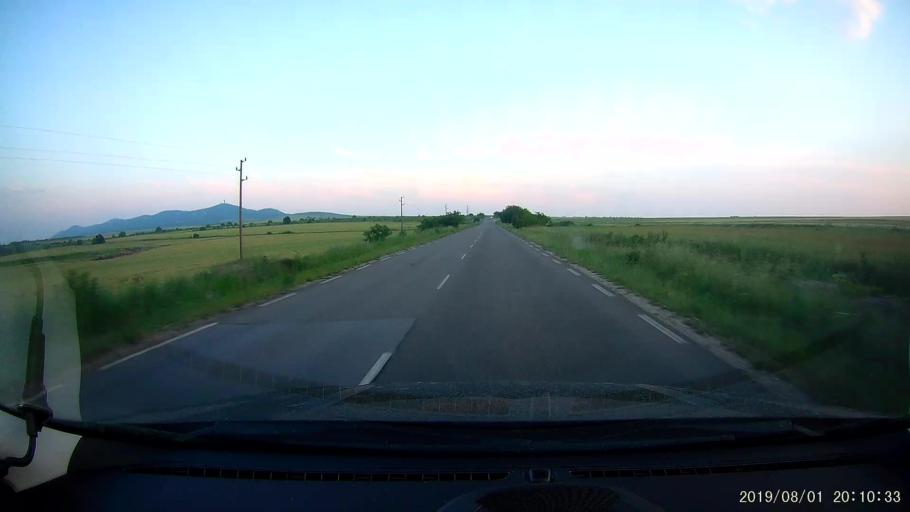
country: BG
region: Yambol
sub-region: Obshtina Yambol
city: Yambol
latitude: 42.4794
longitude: 26.6002
